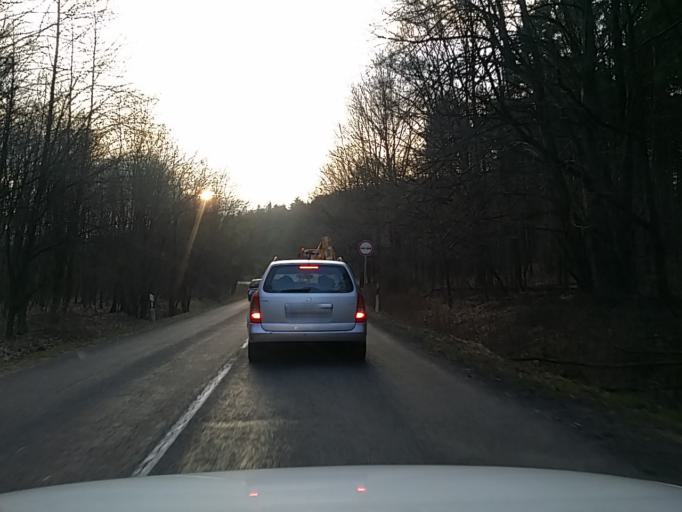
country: HU
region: Nograd
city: Matranovak
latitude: 48.0134
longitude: 20.0175
